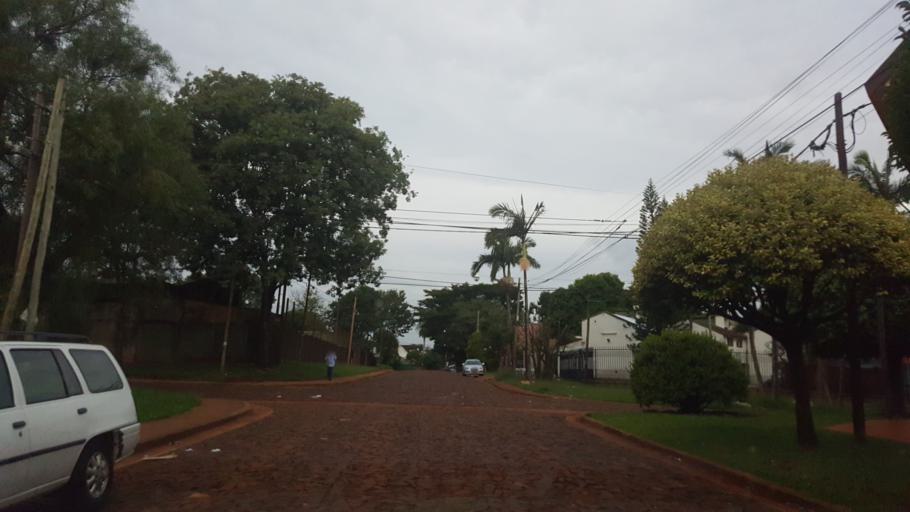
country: AR
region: Misiones
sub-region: Departamento de Capital
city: Posadas
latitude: -27.3940
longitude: -55.9143
